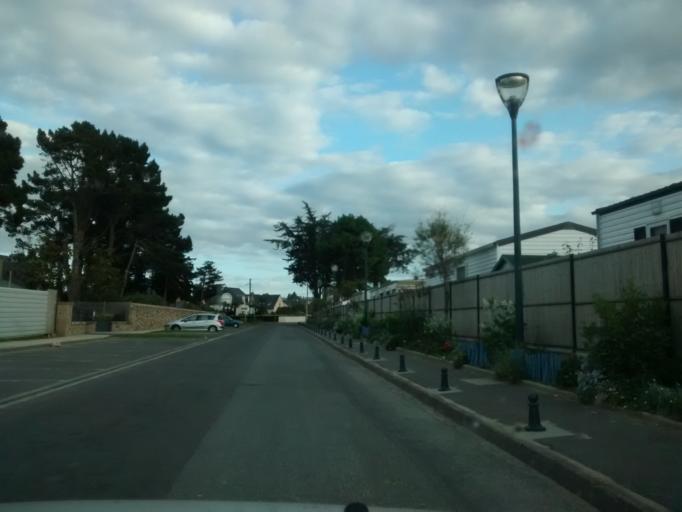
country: FR
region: Brittany
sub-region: Departement d'Ille-et-Vilaine
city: Dinard
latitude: 48.6359
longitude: -2.0793
